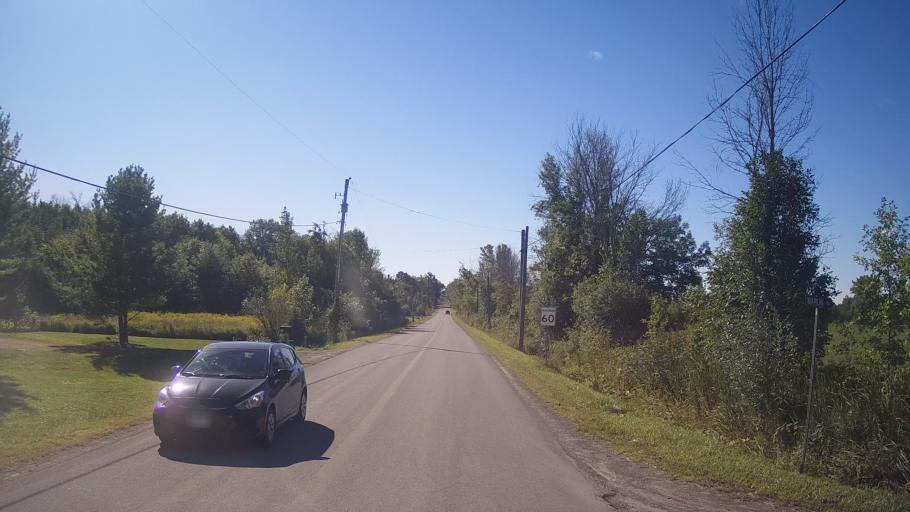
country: CA
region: Ontario
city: Prescott
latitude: 45.0092
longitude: -75.6073
